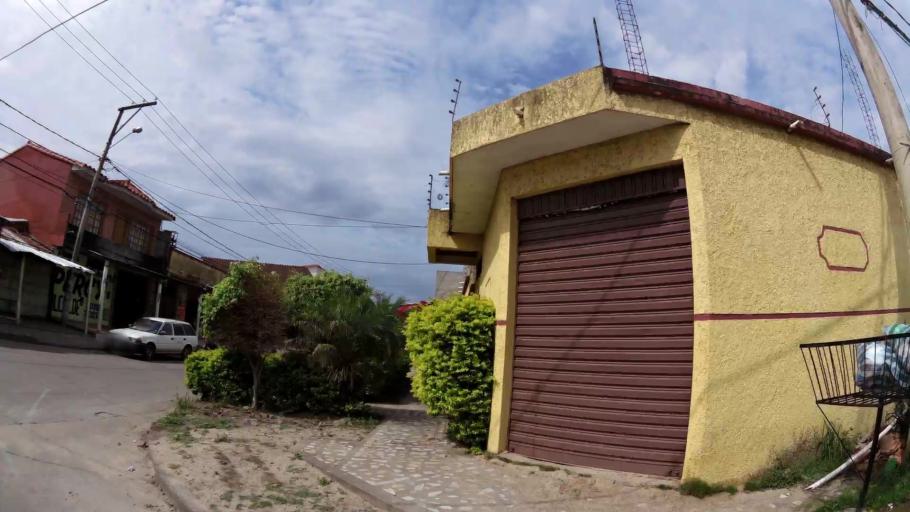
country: BO
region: Santa Cruz
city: Santa Cruz de la Sierra
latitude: -17.7812
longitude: -63.2071
